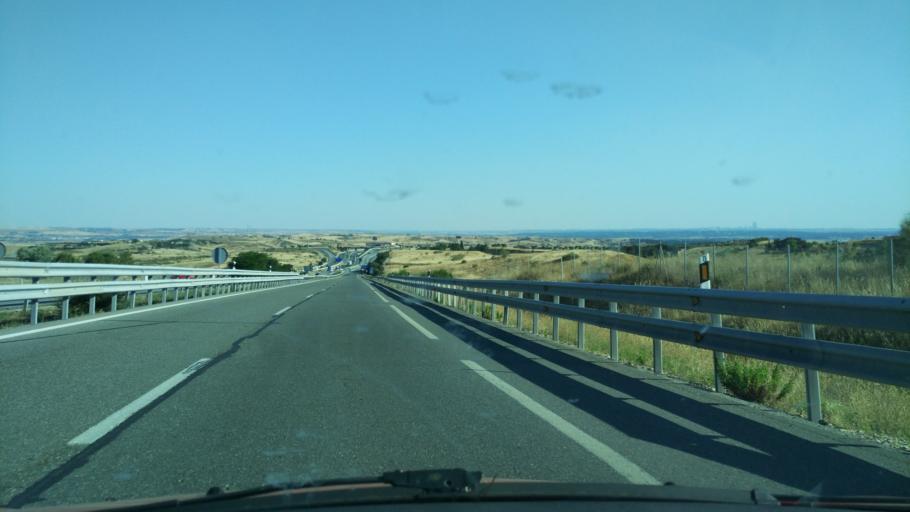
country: ES
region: Madrid
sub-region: Provincia de Madrid
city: El Molar
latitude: 40.7271
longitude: -3.5792
